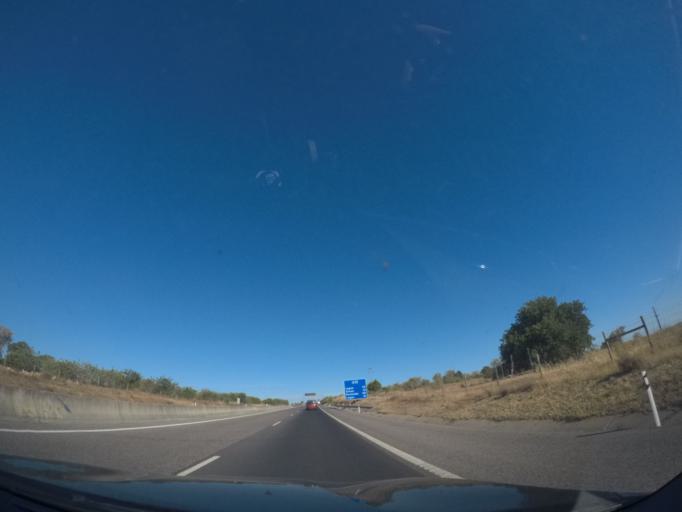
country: PT
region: Faro
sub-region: Silves
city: Armacao de Pera
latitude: 37.1371
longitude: -8.3629
